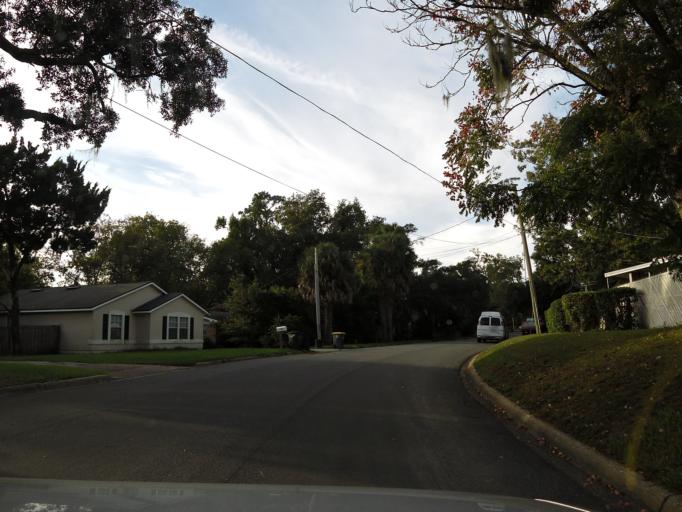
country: US
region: Florida
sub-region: Duval County
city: Jacksonville
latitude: 30.3845
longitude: -81.6612
